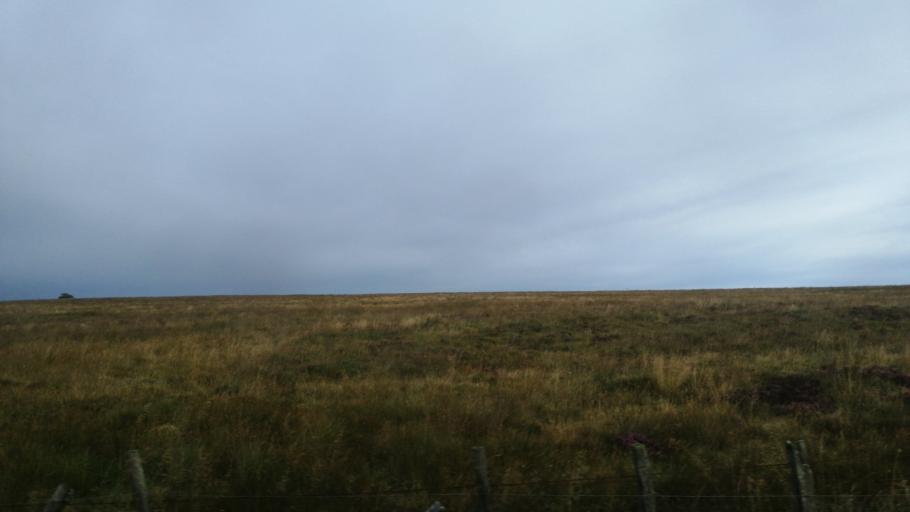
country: GB
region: Scotland
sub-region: Highland
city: Thurso
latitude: 58.4935
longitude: -3.5279
